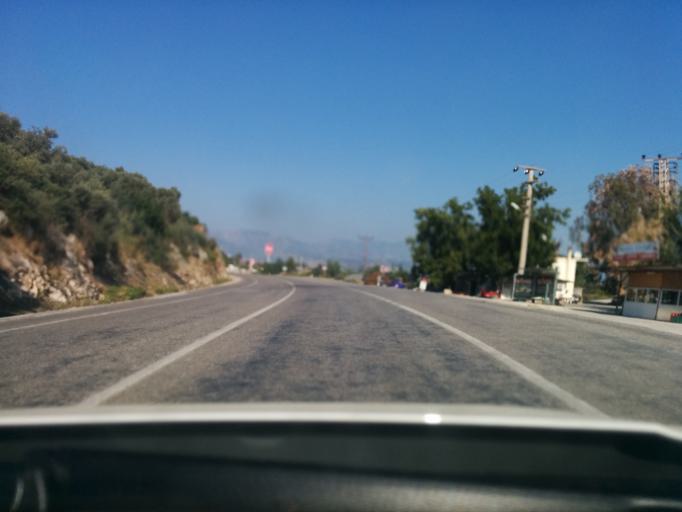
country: TR
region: Antalya
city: Kalkan
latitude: 36.2866
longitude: 29.3528
